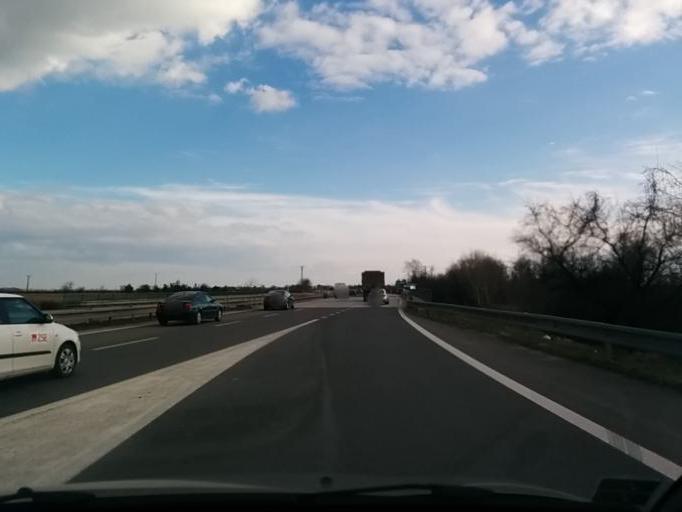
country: SK
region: Trnavsky
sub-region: Okres Trnava
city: Trnava
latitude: 48.3590
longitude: 17.6043
